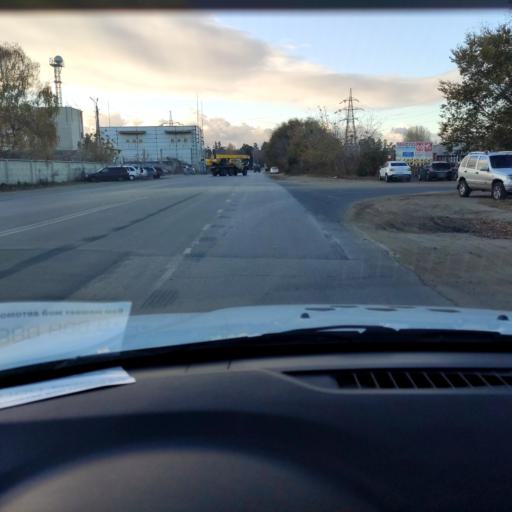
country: RU
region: Samara
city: Zhigulevsk
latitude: 53.5133
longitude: 49.4662
